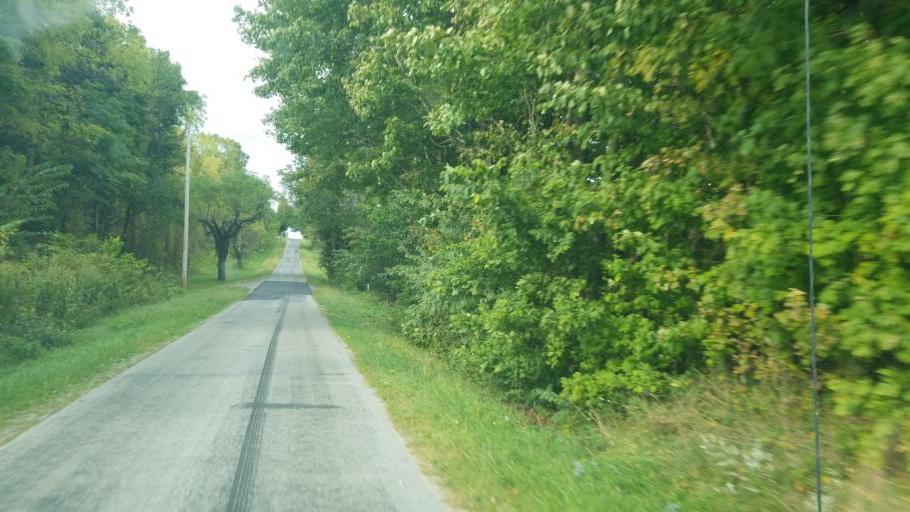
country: US
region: Ohio
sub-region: Wyandot County
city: Upper Sandusky
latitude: 40.8842
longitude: -83.1509
